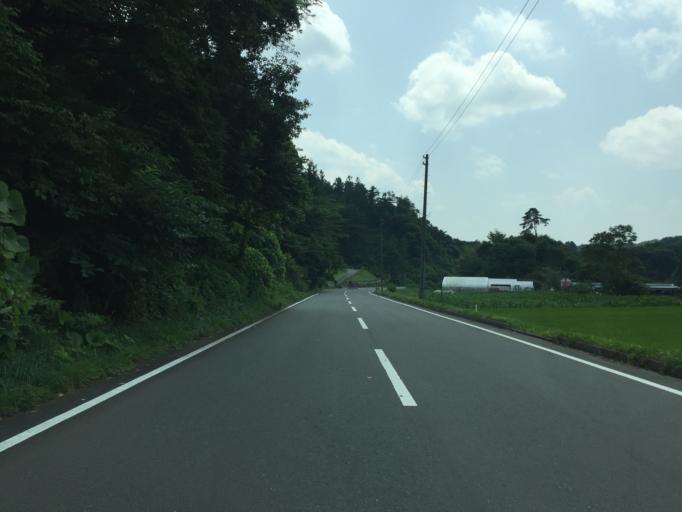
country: JP
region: Fukushima
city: Ishikawa
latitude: 37.2295
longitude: 140.5593
